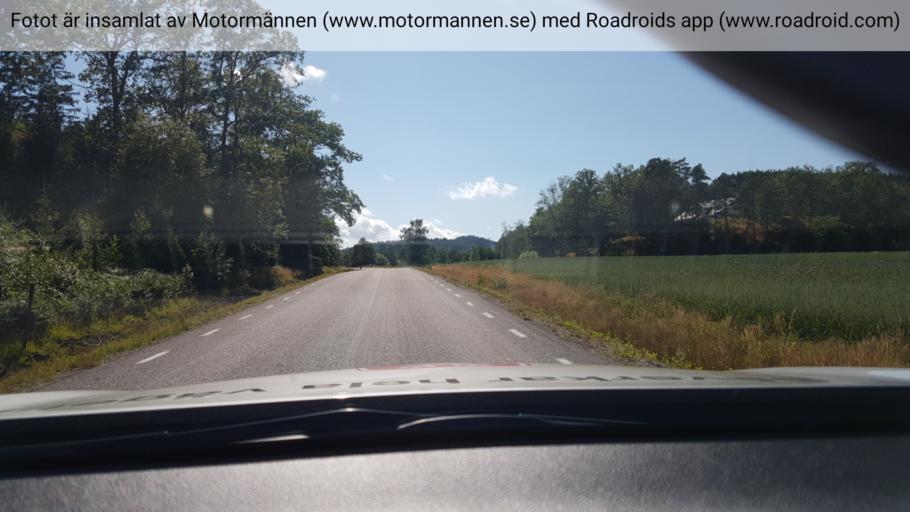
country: SE
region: Vaestra Goetaland
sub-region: Uddevalla Kommun
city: Ljungskile
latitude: 58.2607
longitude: 11.9877
